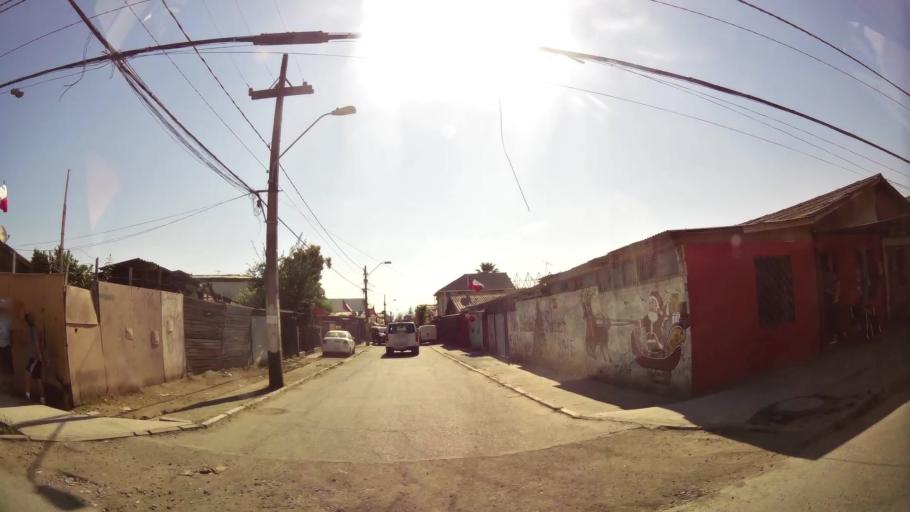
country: CL
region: Santiago Metropolitan
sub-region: Provincia de Santiago
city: Lo Prado
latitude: -33.5142
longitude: -70.6979
